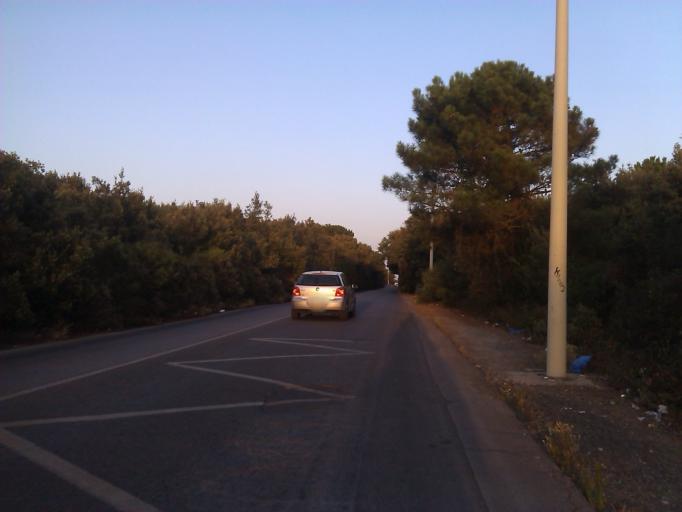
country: IT
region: Latium
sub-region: Citta metropolitana di Roma Capitale
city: Acilia-Castel Fusano-Ostia Antica
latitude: 41.7087
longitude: 12.3343
